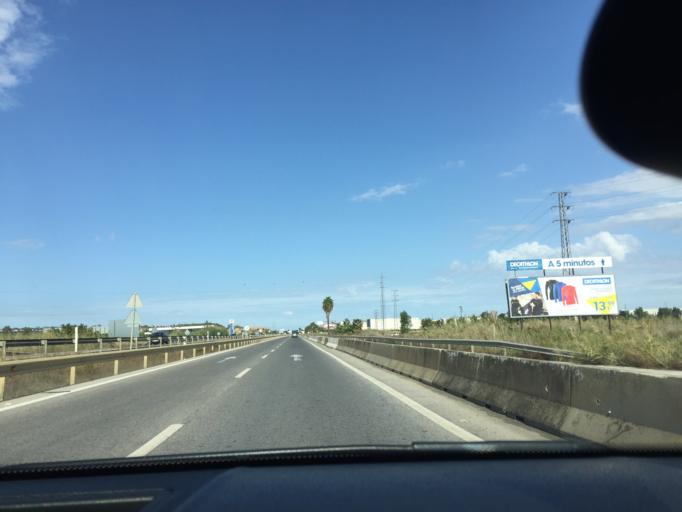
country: ES
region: Andalusia
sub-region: Provincia de Sevilla
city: Palomares del Rio
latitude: 37.3128
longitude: -6.0364
